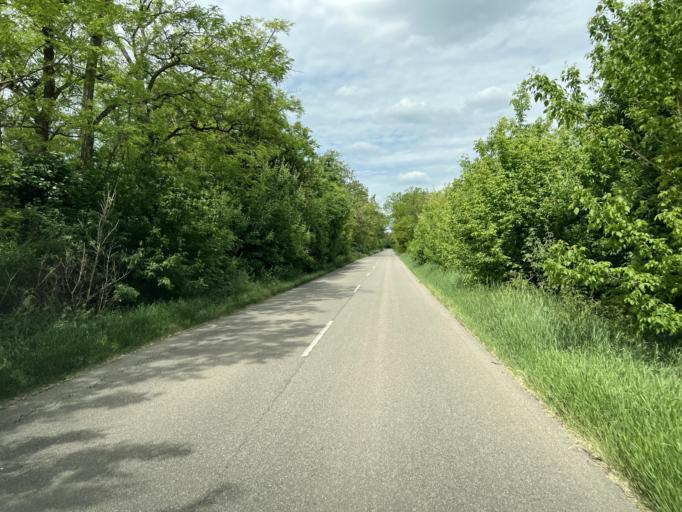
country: HU
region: Pest
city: Zsambok
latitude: 47.5273
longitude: 19.6298
